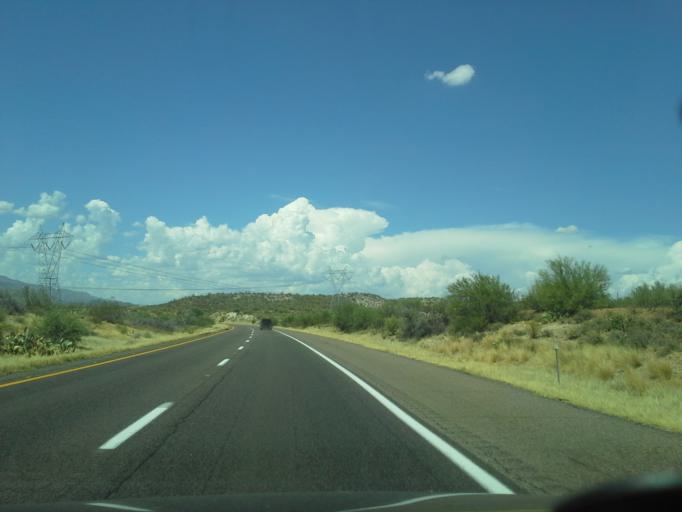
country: US
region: Arizona
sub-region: Yavapai County
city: Black Canyon City
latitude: 34.0063
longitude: -112.1342
